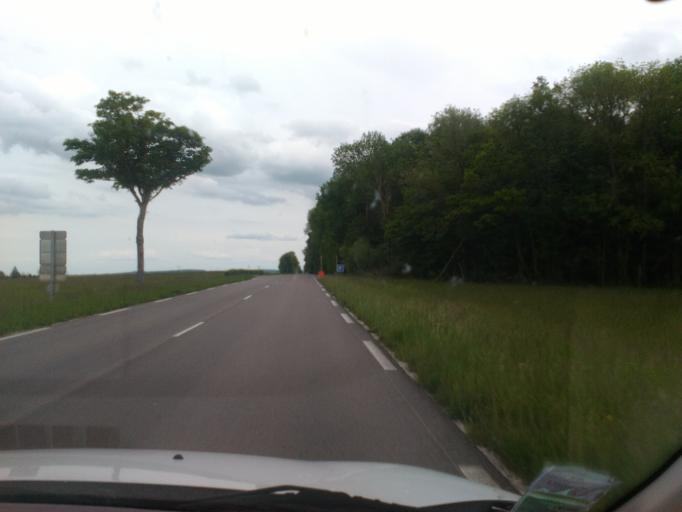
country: FR
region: Champagne-Ardenne
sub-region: Departement de l'Aube
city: Vendeuvre-sur-Barse
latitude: 48.2528
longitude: 4.5708
